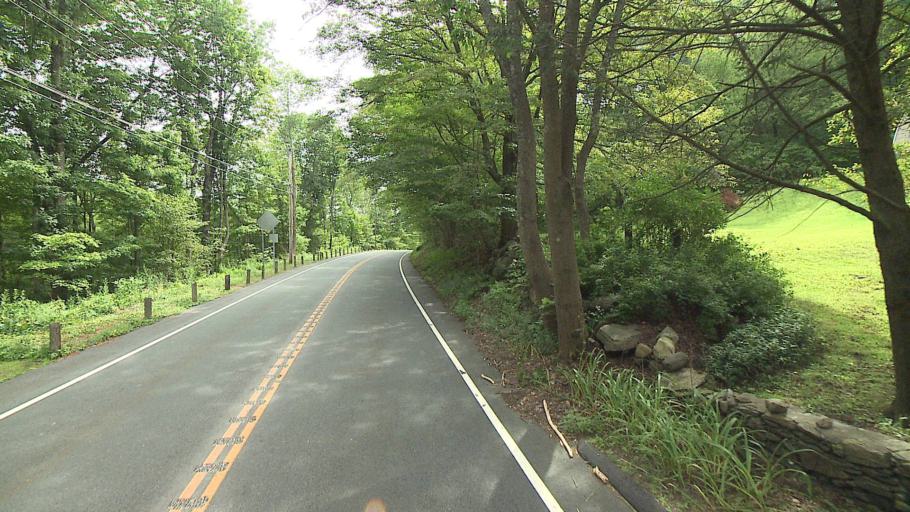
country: US
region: Connecticut
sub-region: Litchfield County
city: New Preston
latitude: 41.7153
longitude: -73.3163
